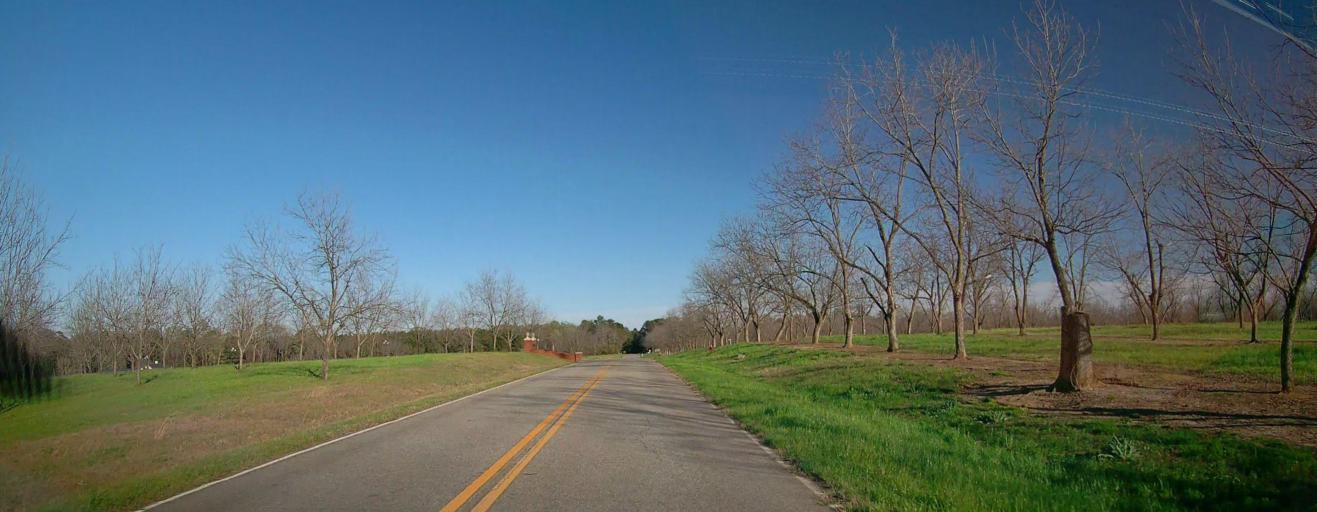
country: US
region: Georgia
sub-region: Houston County
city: Perry
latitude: 32.3657
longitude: -83.6773
